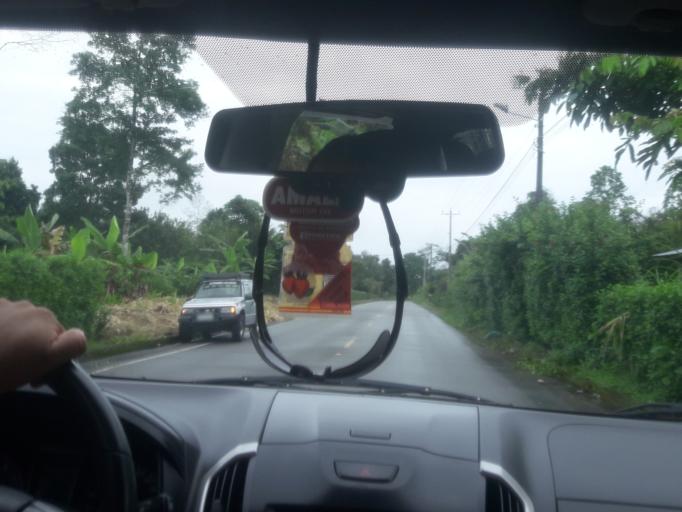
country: EC
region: Napo
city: Tena
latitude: -1.0433
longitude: -77.6980
